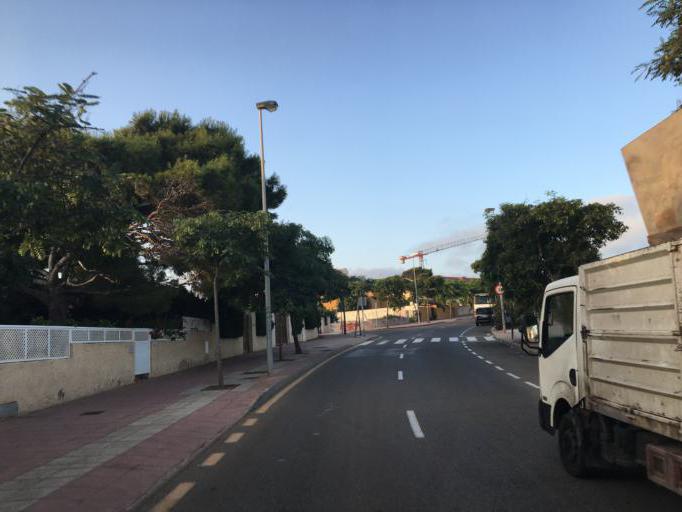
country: ES
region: Murcia
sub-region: Murcia
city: La Manga del Mar Menor
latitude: 37.6267
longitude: -0.7062
